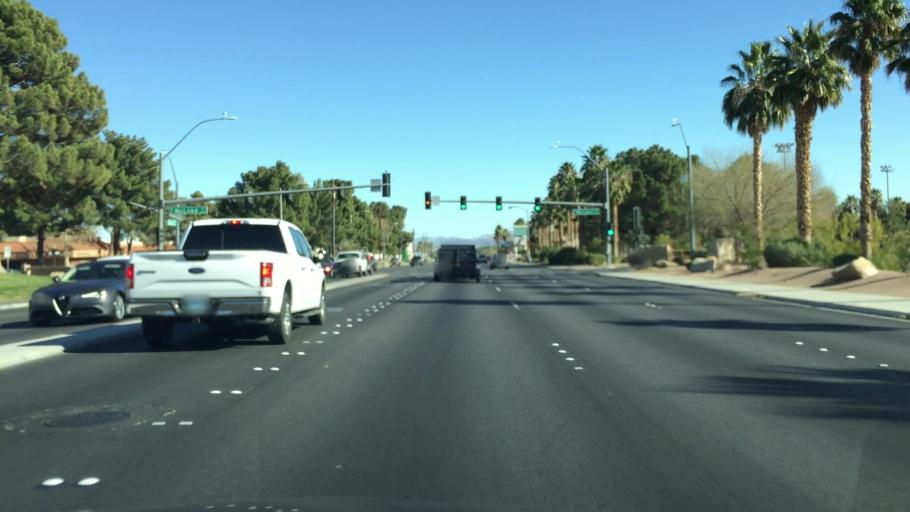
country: US
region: Nevada
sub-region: Clark County
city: Whitney
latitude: 36.0715
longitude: -115.1136
